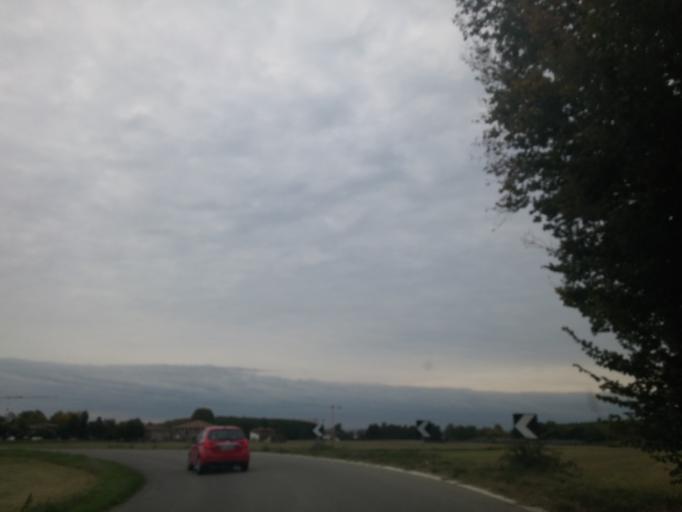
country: IT
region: Emilia-Romagna
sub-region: Provincia di Bologna
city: Longara
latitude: 44.5821
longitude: 11.3222
